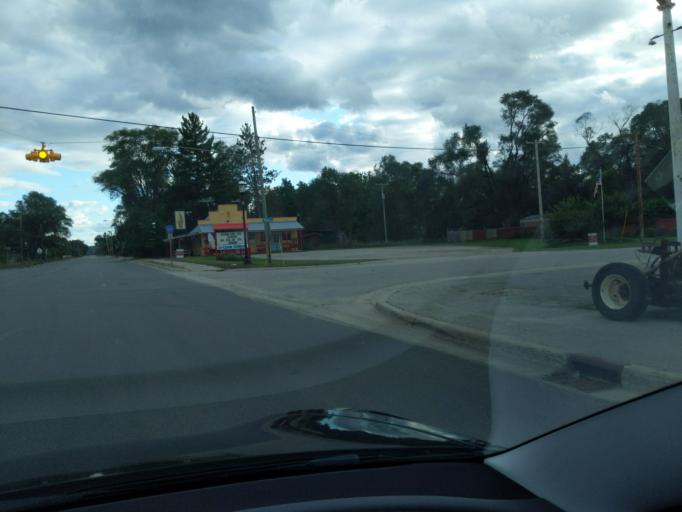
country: US
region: Michigan
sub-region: Kalkaska County
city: Rapid City
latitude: 44.8337
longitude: -85.2828
